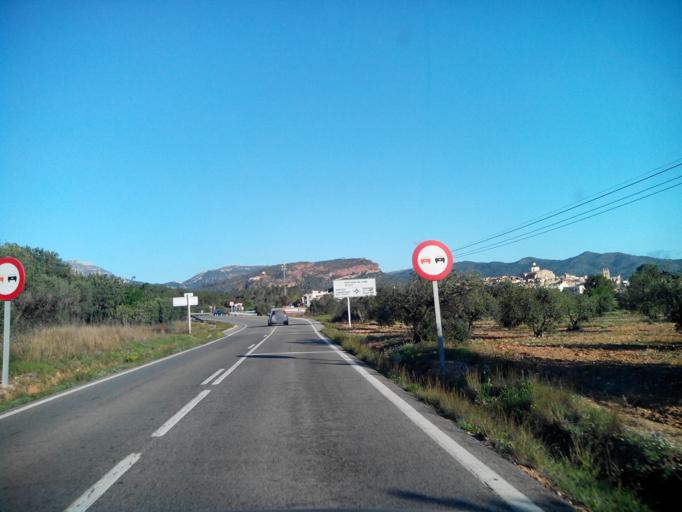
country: ES
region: Catalonia
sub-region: Provincia de Tarragona
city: Vilanova d'Escornalbou
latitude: 41.0802
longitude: 0.9635
